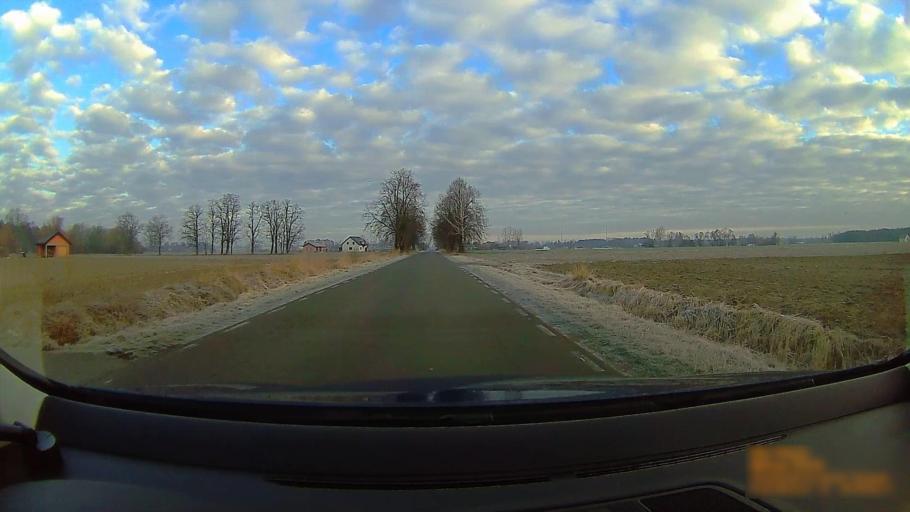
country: PL
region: Greater Poland Voivodeship
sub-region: Powiat koninski
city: Rzgow Pierwszy
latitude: 52.1403
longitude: 18.0564
